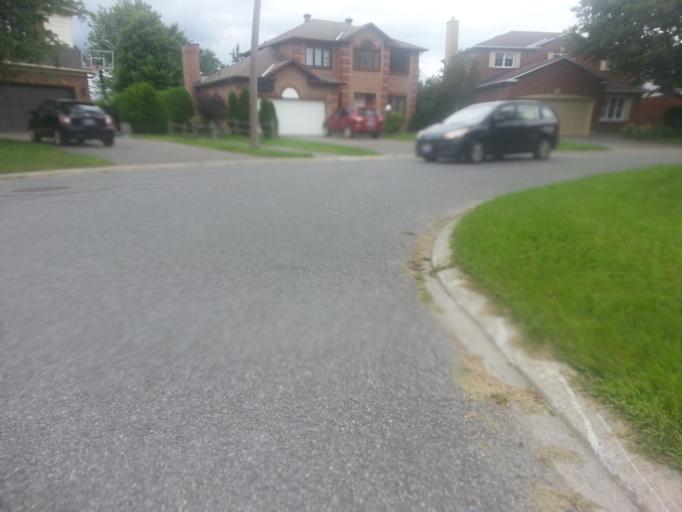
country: CA
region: Ontario
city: Bells Corners
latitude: 45.3303
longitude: -75.9167
